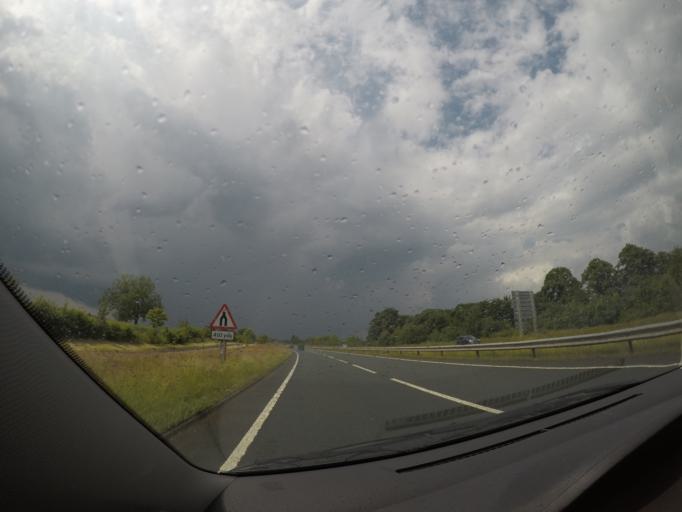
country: GB
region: England
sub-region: Cumbria
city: Penrith
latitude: 54.6507
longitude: -2.6311
